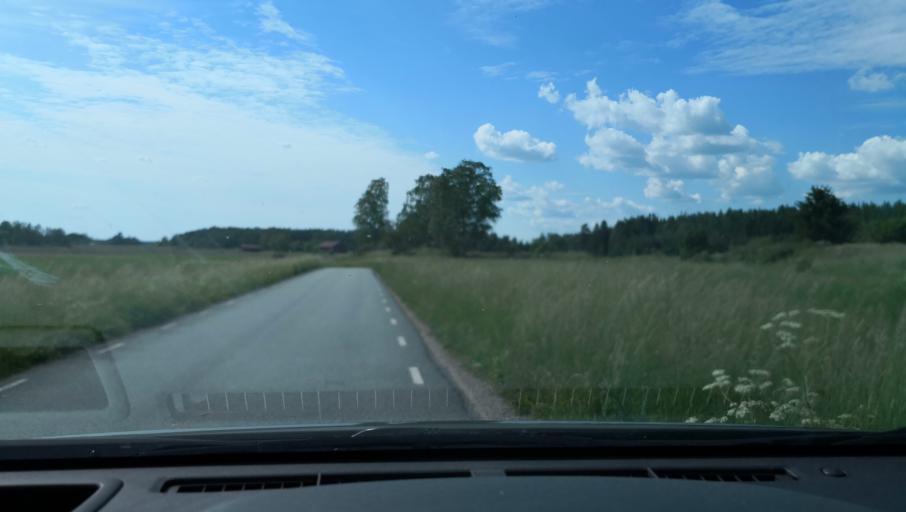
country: SE
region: Uppsala
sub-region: Enkopings Kommun
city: Orsundsbro
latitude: 59.8160
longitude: 17.3546
